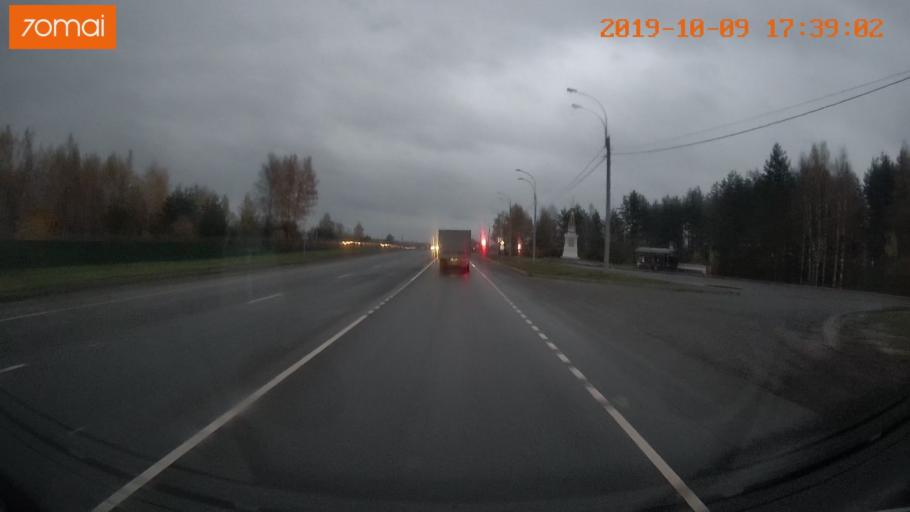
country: RU
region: Ivanovo
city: Bogorodskoye
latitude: 57.0643
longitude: 40.9538
